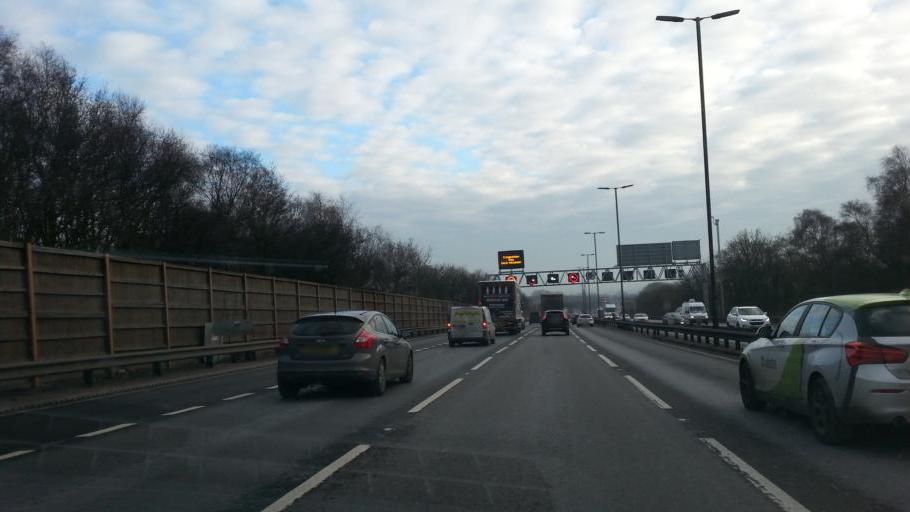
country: GB
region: England
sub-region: City and Borough of Birmingham
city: Hockley
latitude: 52.5494
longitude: -1.9213
